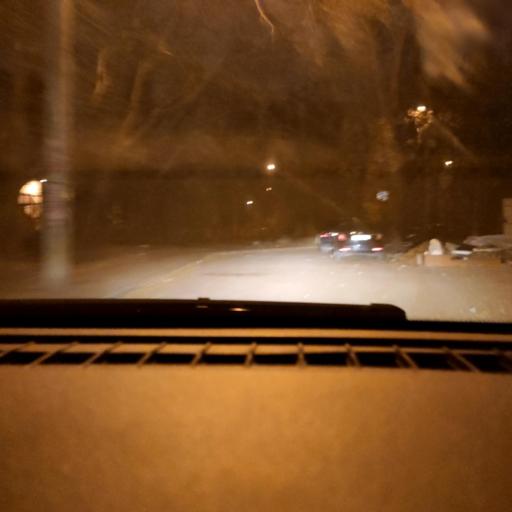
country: RU
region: Voronezj
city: Voronezh
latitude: 51.7004
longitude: 39.1872
